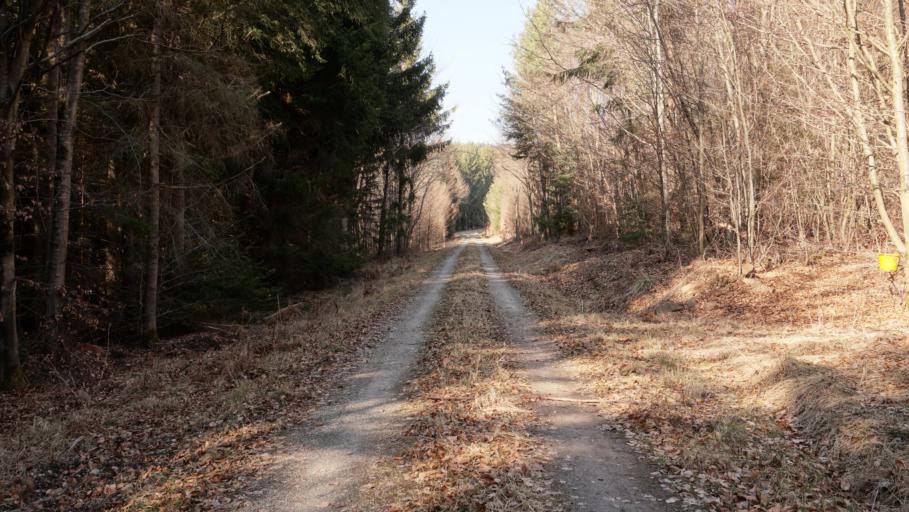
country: DE
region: Baden-Wuerttemberg
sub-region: Karlsruhe Region
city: Fahrenbach
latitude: 49.4489
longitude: 9.1280
